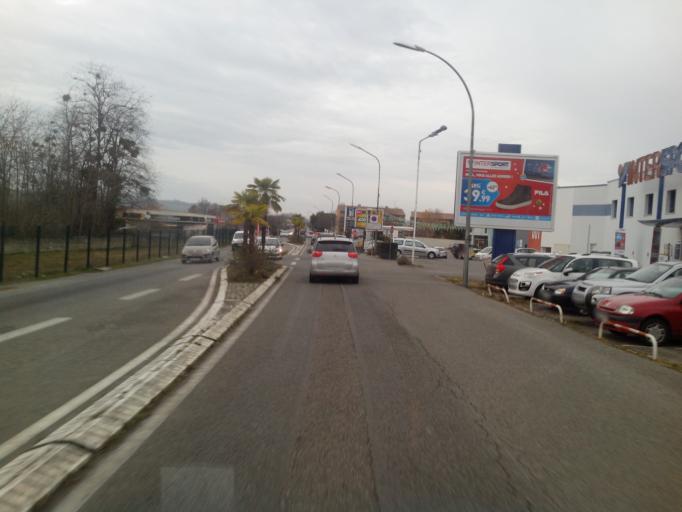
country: FR
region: Midi-Pyrenees
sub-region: Departement de l'Ariege
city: Saint-Jean-du-Falga
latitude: 43.1002
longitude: 1.6238
